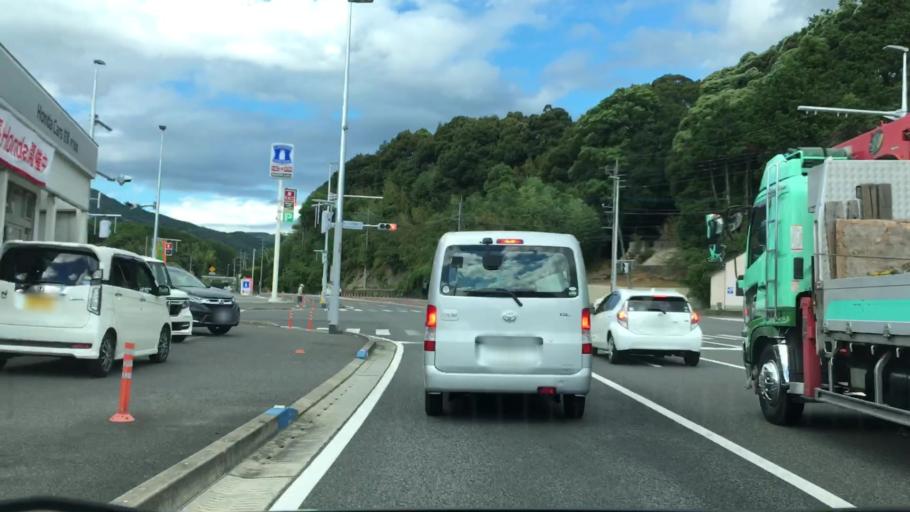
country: JP
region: Saga Prefecture
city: Imaricho-ko
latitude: 33.2770
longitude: 129.8946
